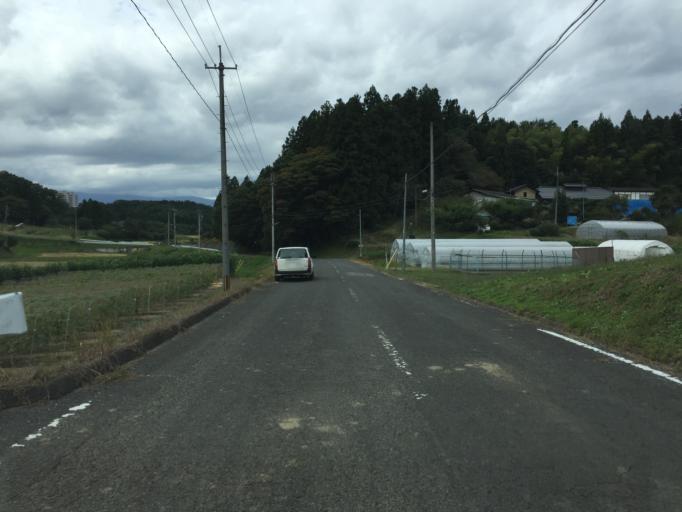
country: JP
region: Fukushima
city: Fukushima-shi
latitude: 37.6883
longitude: 140.4859
